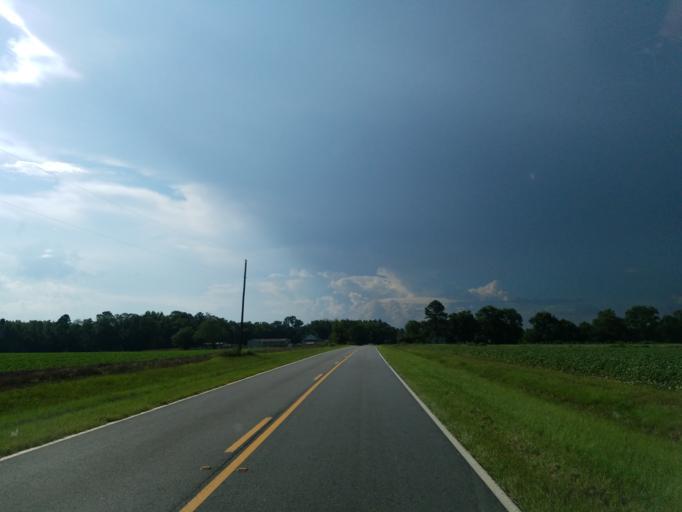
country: US
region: Georgia
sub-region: Lowndes County
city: Hahira
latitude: 31.0295
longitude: -83.4419
